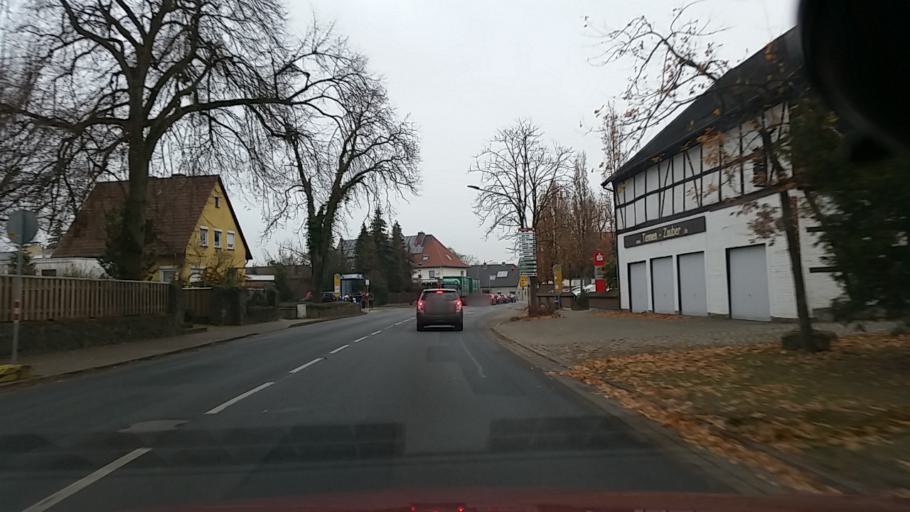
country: DE
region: Lower Saxony
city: Wittingen
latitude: 52.7277
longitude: 10.7366
